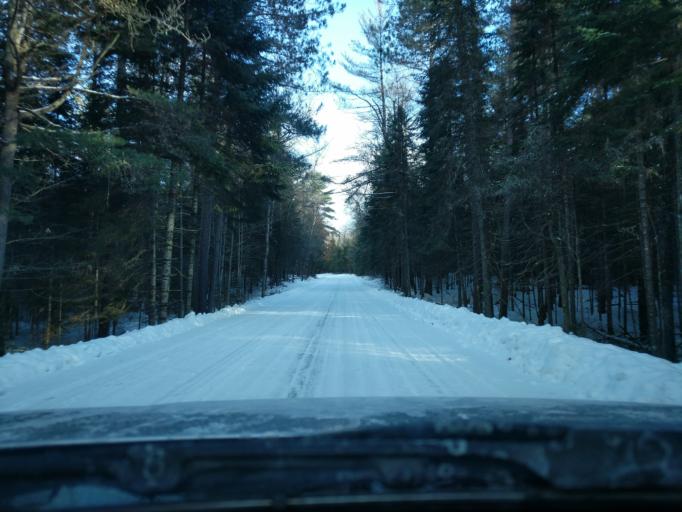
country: US
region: Wisconsin
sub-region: Vilas County
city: Eagle River
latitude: 45.8114
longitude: -89.0473
